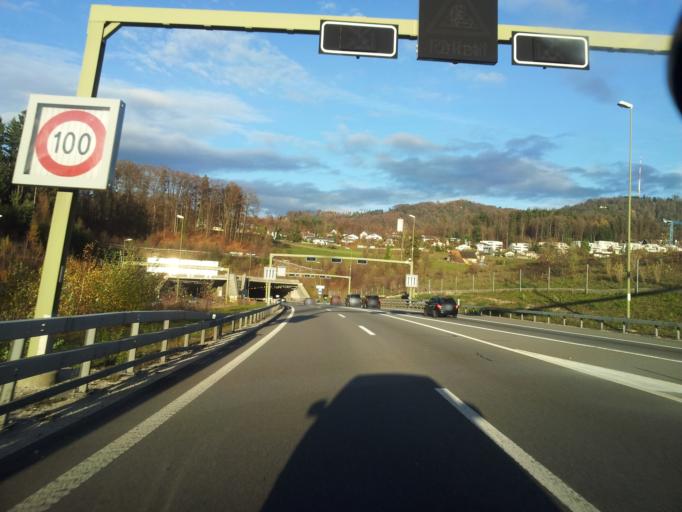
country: CH
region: Zurich
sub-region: Bezirk Affoltern
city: Wettswil / Wettswil (Dorf)
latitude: 47.3428
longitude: 8.4594
